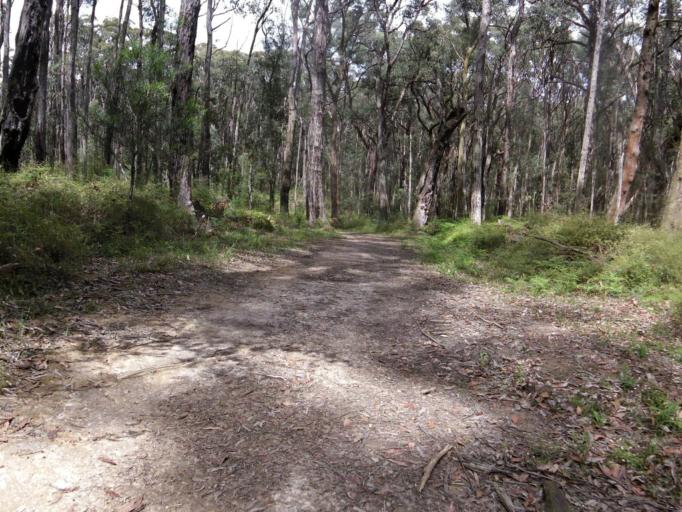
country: AU
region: Victoria
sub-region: Cardinia
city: Cockatoo
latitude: -37.9280
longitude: 145.4815
